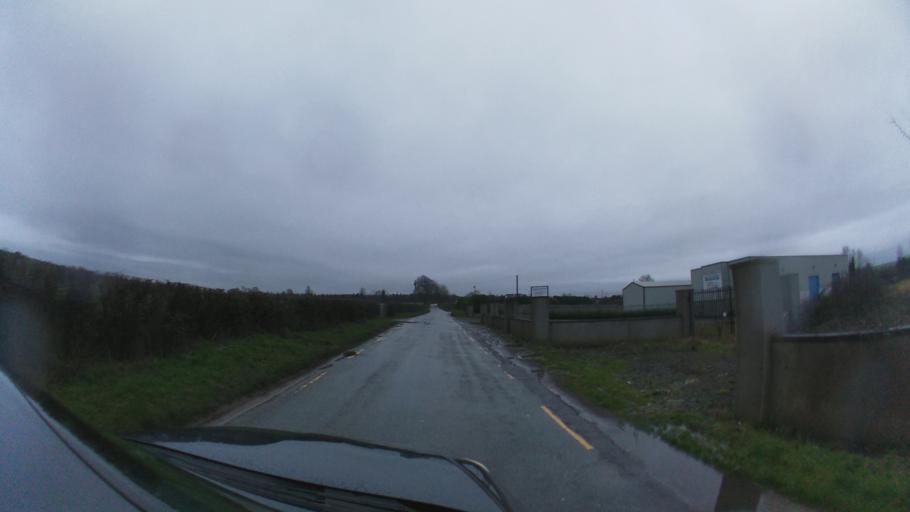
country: IE
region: Leinster
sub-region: County Carlow
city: Bagenalstown
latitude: 52.6260
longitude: -6.9918
